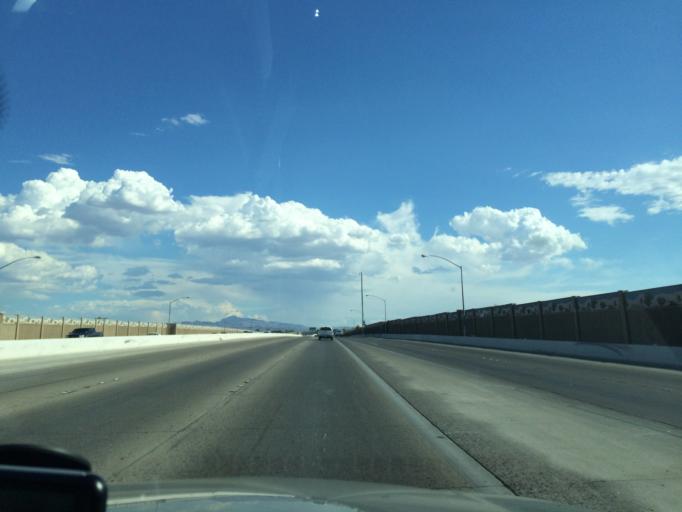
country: US
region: Nevada
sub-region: Clark County
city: Winchester
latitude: 36.1537
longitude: -115.0917
